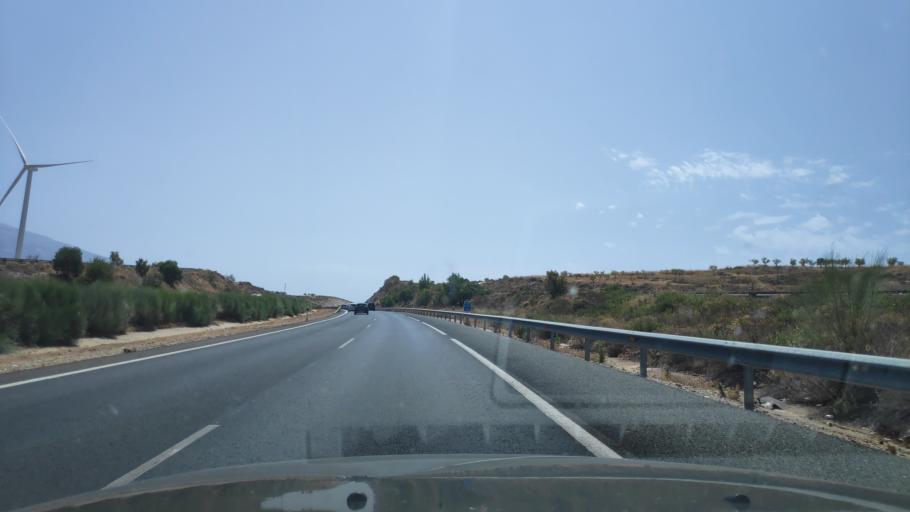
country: ES
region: Andalusia
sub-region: Provincia de Granada
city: Padul
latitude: 37.0051
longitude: -3.6372
